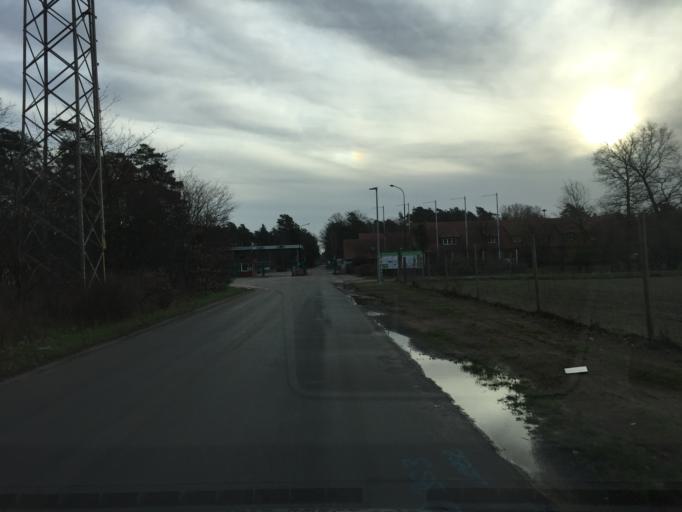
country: DE
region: Lower Saxony
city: Leese
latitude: 52.5257
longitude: 9.1292
